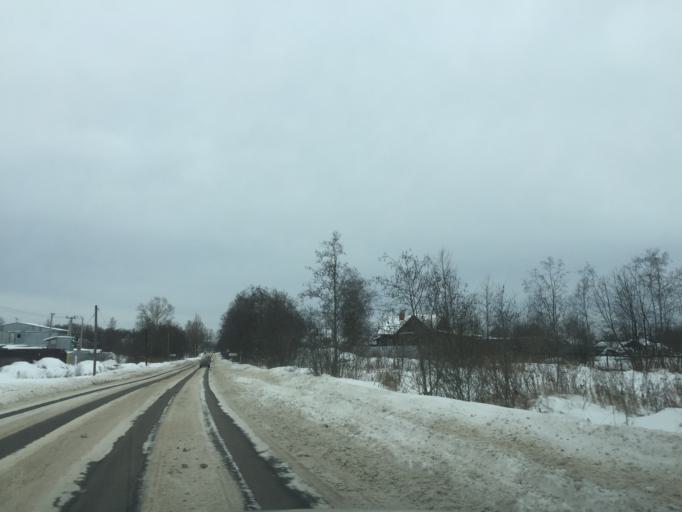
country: RU
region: Leningrad
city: Imeni Sverdlova
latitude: 59.7920
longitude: 30.6786
